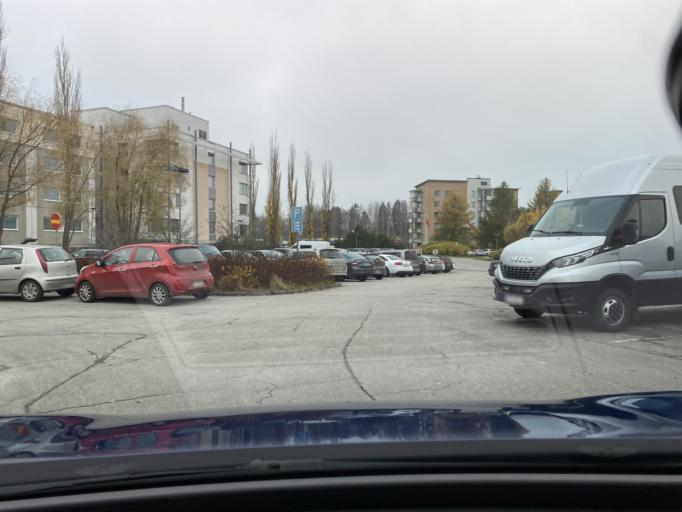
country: FI
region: Pirkanmaa
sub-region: Tampere
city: Nokia
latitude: 61.4682
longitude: 23.5301
